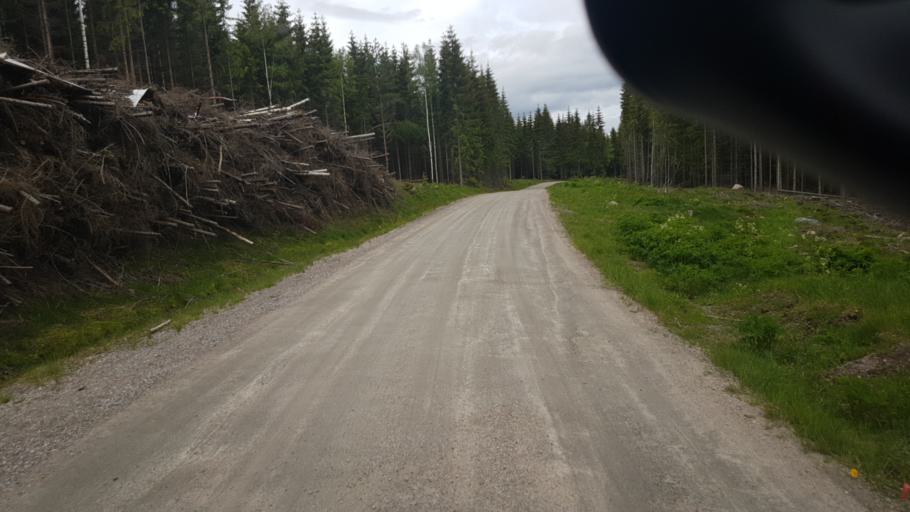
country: SE
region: Vaermland
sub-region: Eda Kommun
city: Amotfors
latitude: 59.8444
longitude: 12.5244
